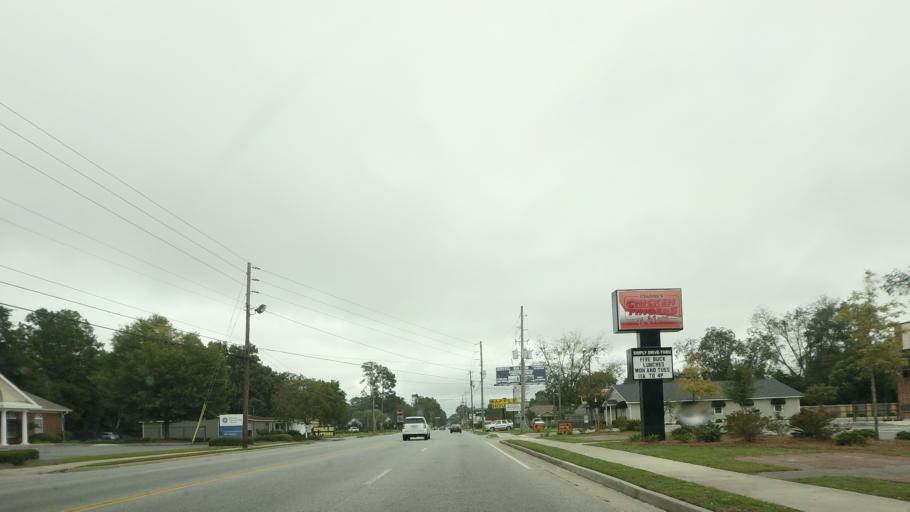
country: US
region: Georgia
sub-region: Lowndes County
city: Remerton
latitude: 30.8468
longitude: -83.3065
